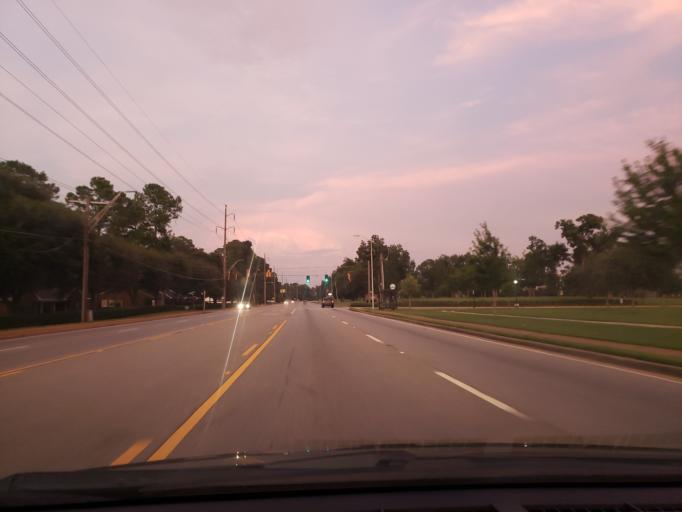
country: US
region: Georgia
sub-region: Dougherty County
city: Albany
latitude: 31.5857
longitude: -84.2152
